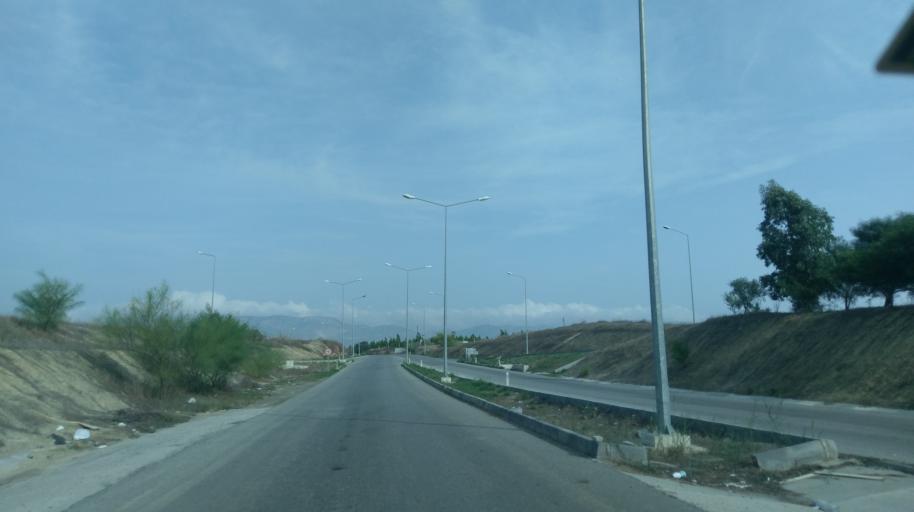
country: CY
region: Lefkosia
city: Mammari
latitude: 35.2177
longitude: 33.1795
